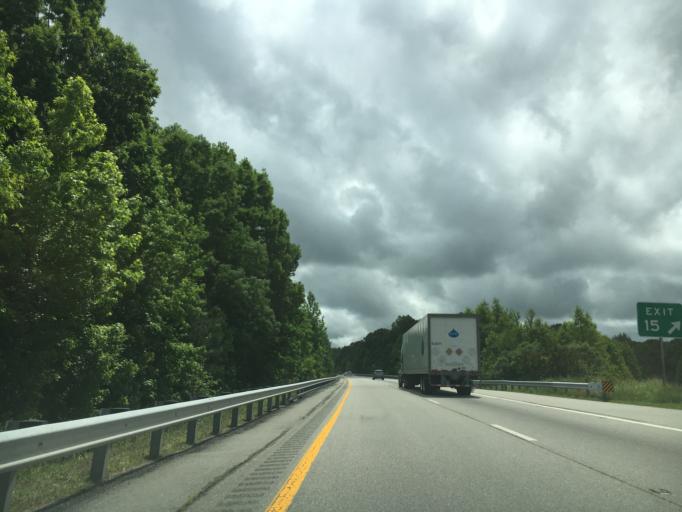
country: US
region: Virginia
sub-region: Mecklenburg County
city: South Hill
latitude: 36.7531
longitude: -78.0931
